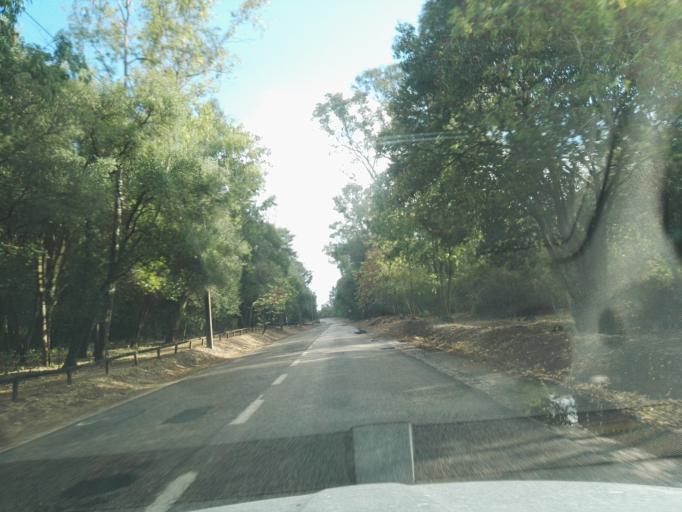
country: PT
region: Lisbon
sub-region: Amadora
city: Amadora
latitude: 38.7296
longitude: -9.2041
